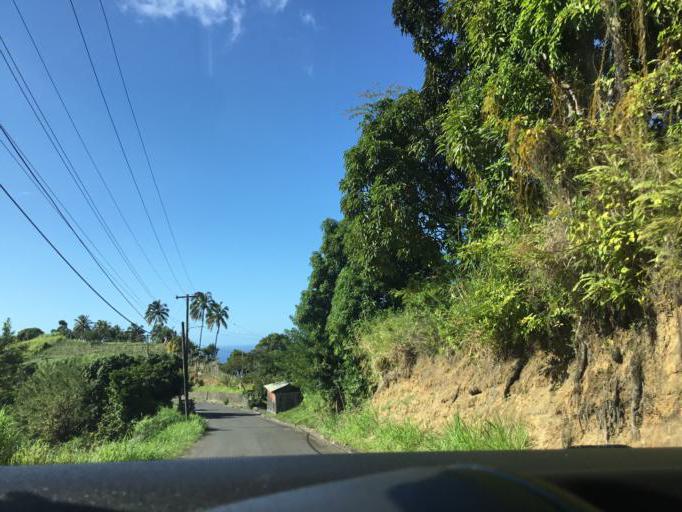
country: VC
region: Saint David
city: Chateaubelair
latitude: 13.2739
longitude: -61.2440
